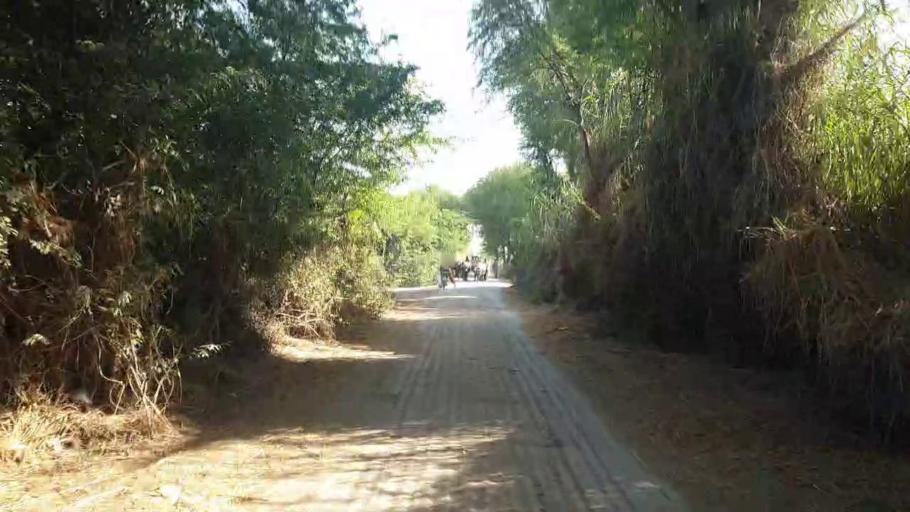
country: PK
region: Sindh
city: Matli
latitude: 25.0251
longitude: 68.7342
